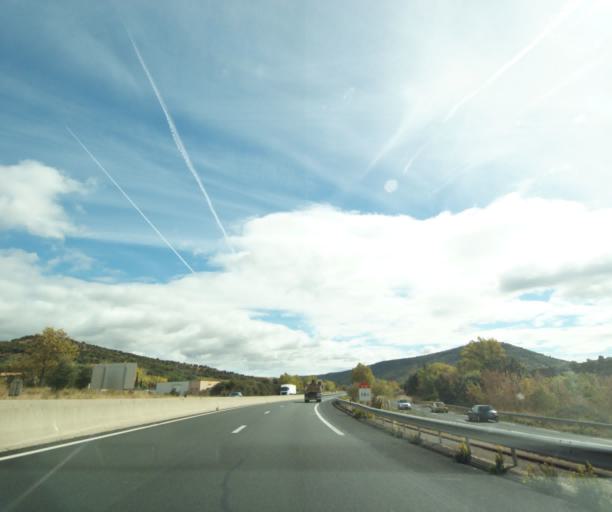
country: FR
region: Languedoc-Roussillon
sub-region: Departement de l'Herault
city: Lodeve
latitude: 43.6917
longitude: 3.3484
